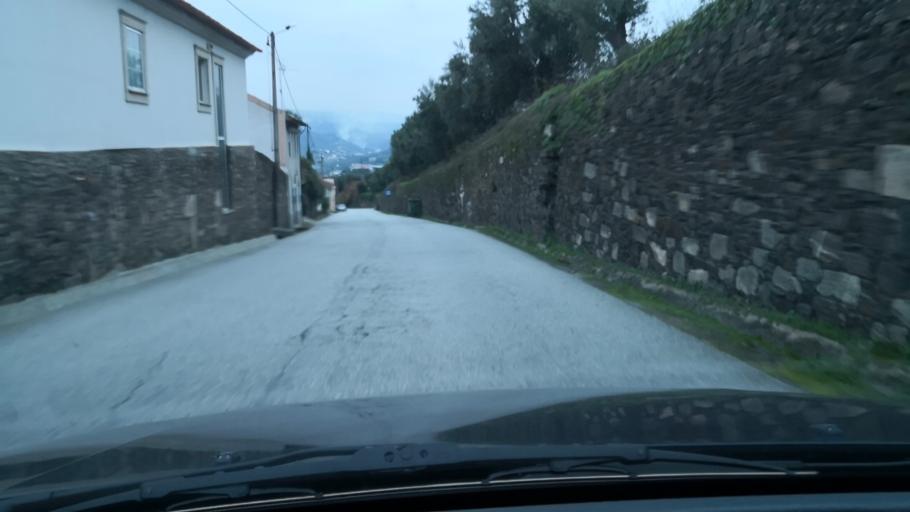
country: PT
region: Vila Real
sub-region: Peso da Regua
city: Peso da Regua
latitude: 41.1470
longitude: -7.7922
